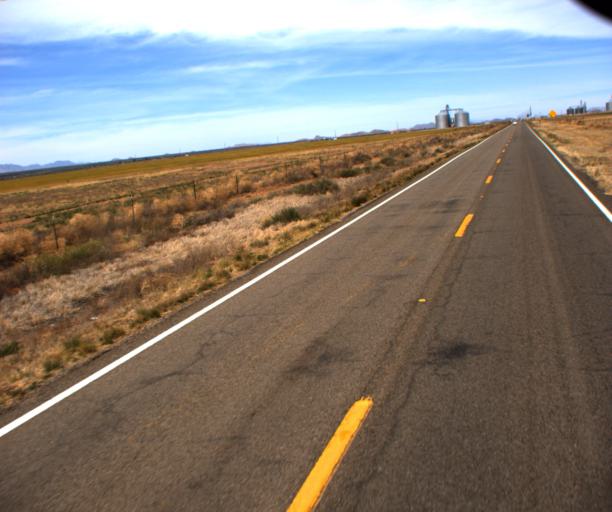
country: US
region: Arizona
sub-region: Cochise County
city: Tombstone
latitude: 31.7494
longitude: -109.6887
